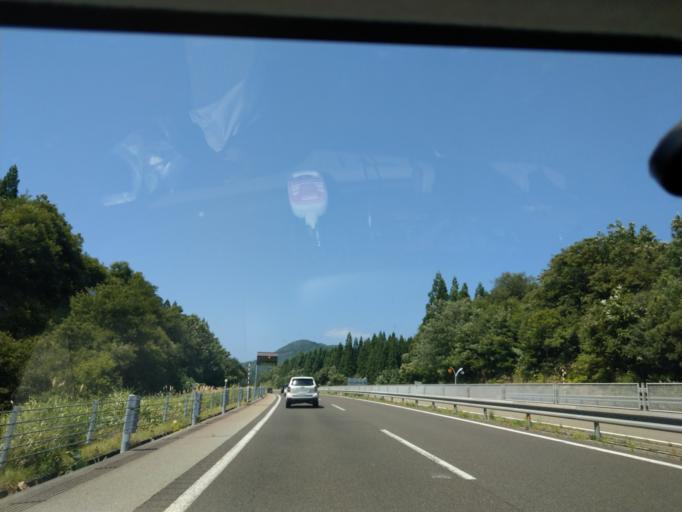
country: JP
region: Akita
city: Omagari
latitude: 39.4236
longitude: 140.4318
